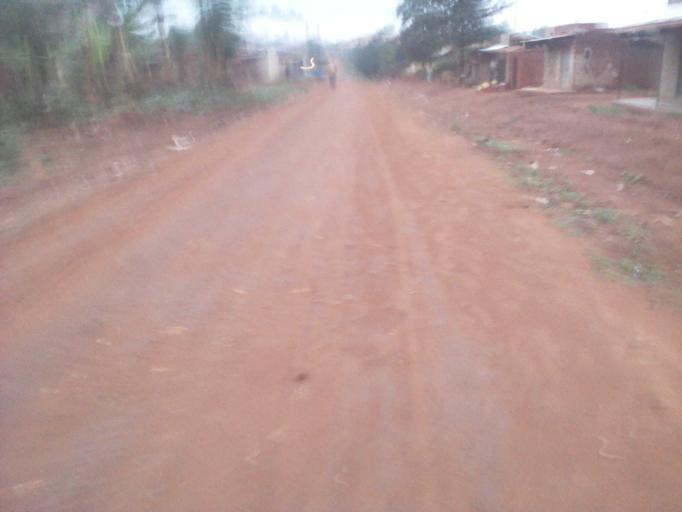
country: UG
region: Eastern Region
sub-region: Mbale District
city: Mbale
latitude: 1.0858
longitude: 34.1750
